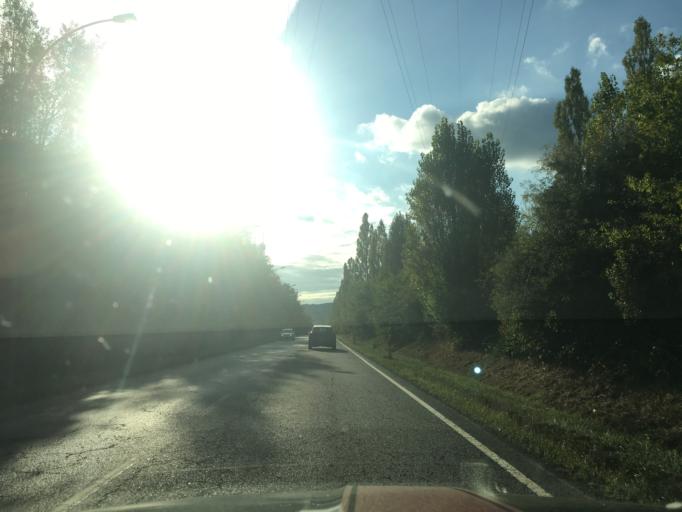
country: LU
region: Luxembourg
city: Belvaux
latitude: 49.5237
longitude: 5.9161
